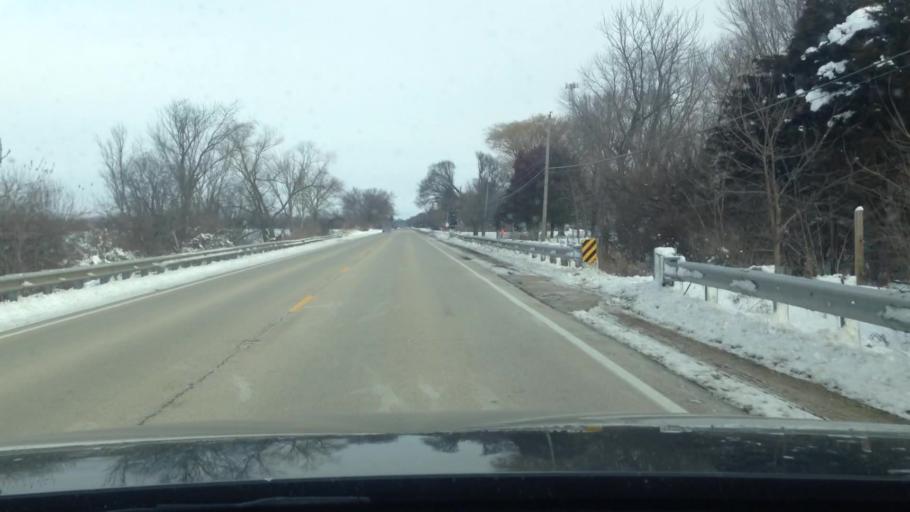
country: US
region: Illinois
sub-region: McHenry County
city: Woodstock
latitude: 42.3715
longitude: -88.4431
